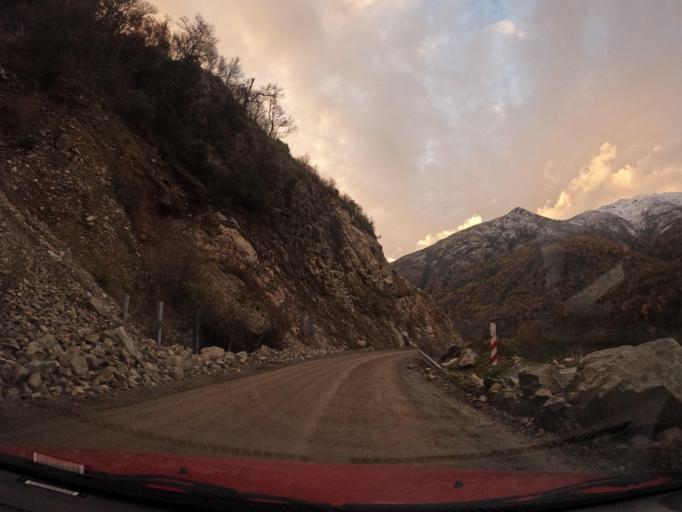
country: CL
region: Maule
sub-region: Provincia de Linares
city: Colbun
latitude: -35.8593
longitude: -71.1610
